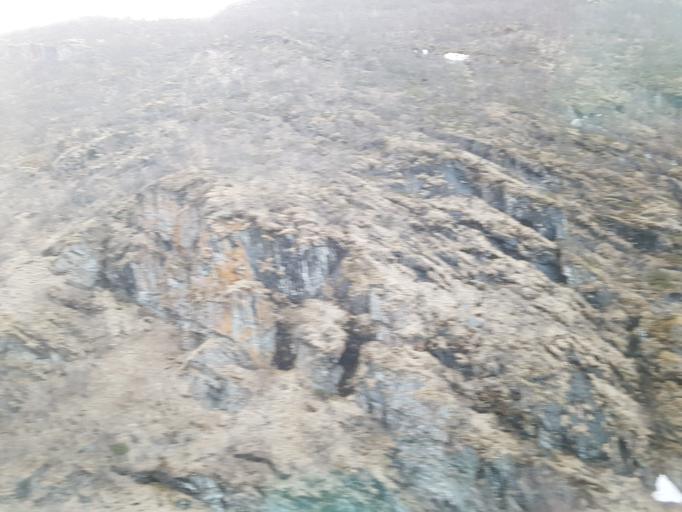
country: NO
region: Sor-Trondelag
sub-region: Oppdal
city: Oppdal
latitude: 62.3405
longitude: 9.6186
